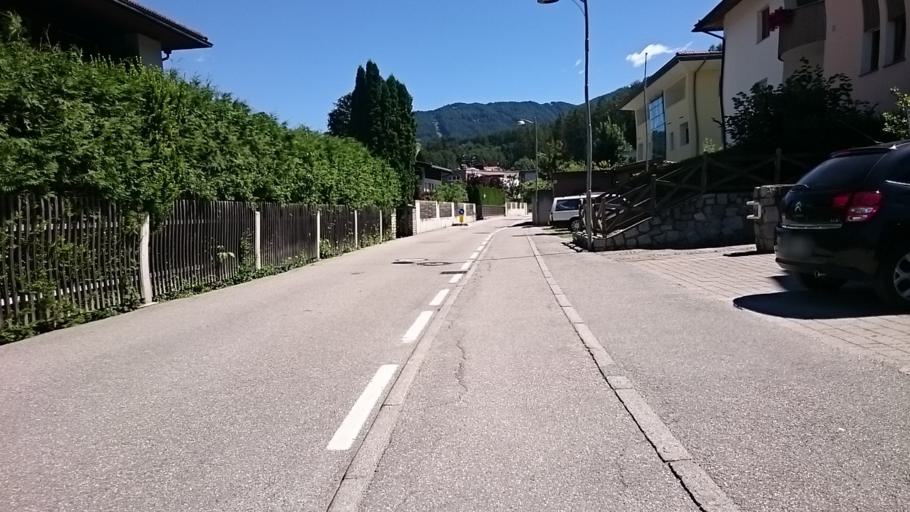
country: IT
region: Trentino-Alto Adige
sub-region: Bolzano
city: Brunico
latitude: 46.7923
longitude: 11.9452
